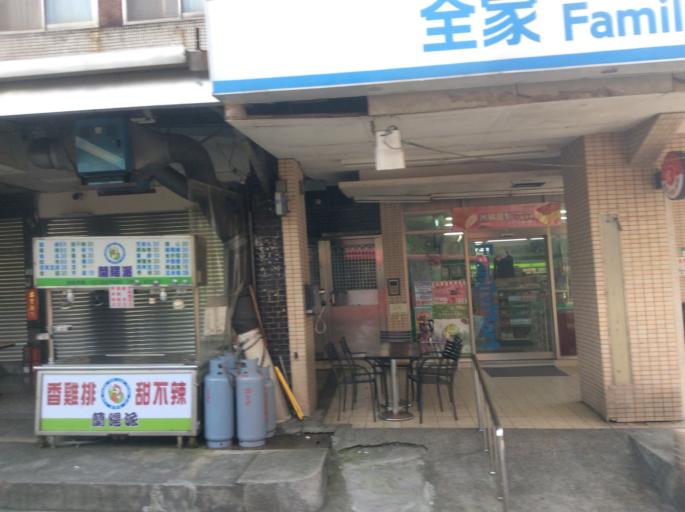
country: TW
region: Taipei
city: Taipei
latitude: 25.1367
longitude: 121.5464
